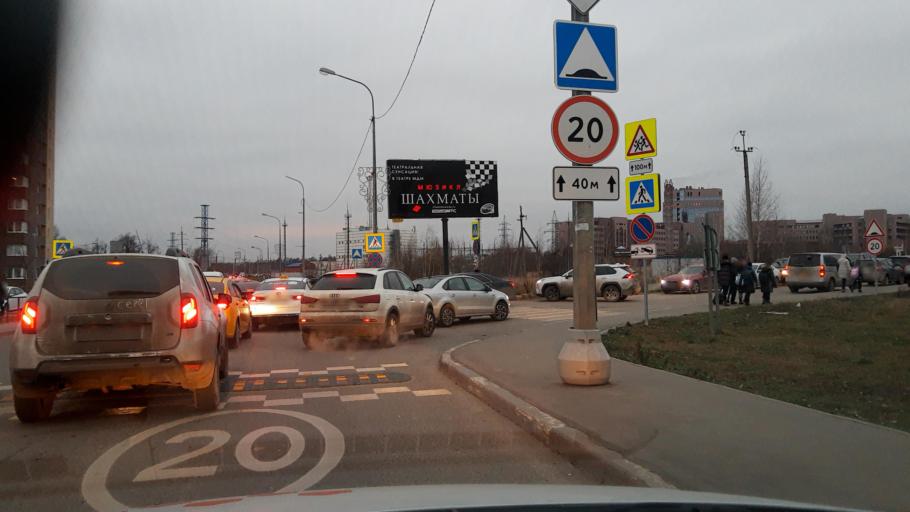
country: RU
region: Moskovskaya
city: Kommunarka
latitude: 55.5777
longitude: 37.4760
